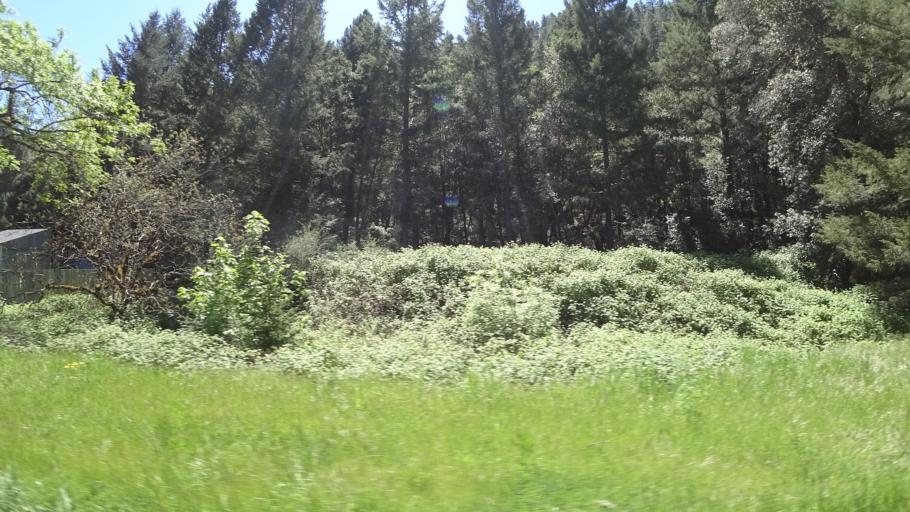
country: US
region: California
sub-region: Humboldt County
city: Willow Creek
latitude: 40.8715
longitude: -123.5272
